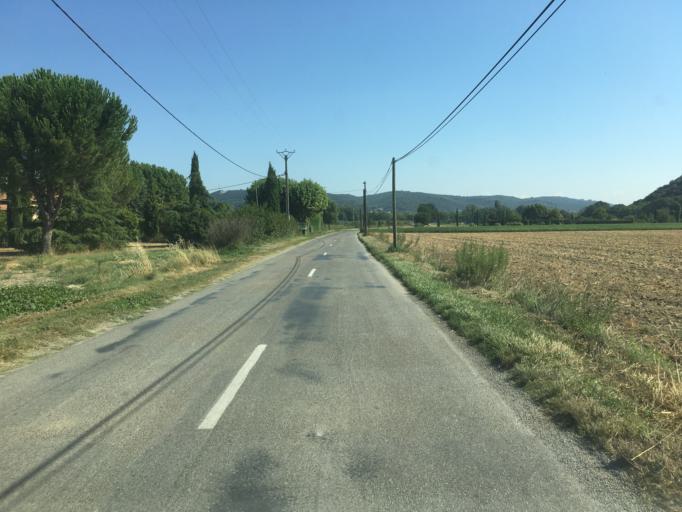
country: FR
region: Provence-Alpes-Cote d'Azur
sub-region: Departement des Alpes-de-Haute-Provence
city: Oraison
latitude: 43.8730
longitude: 5.9029
